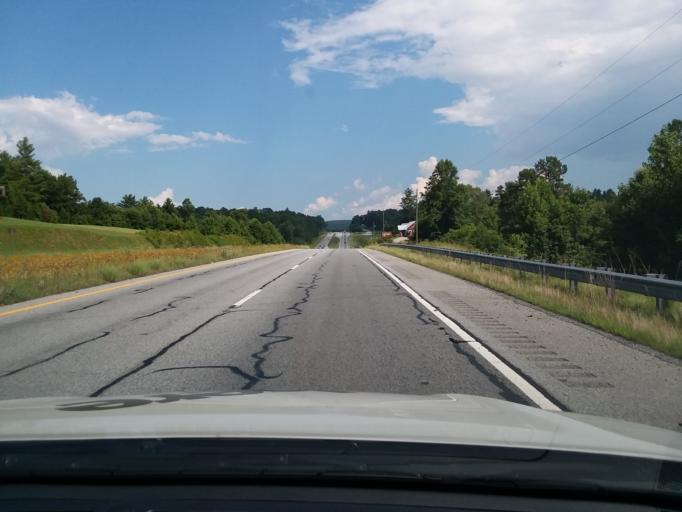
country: US
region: Georgia
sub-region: Rabun County
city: Clayton
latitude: 34.7963
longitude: -83.4164
